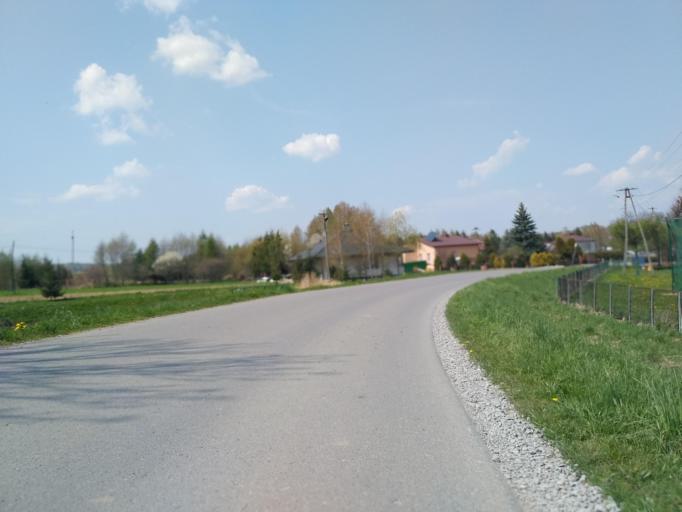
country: PL
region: Subcarpathian Voivodeship
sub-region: Powiat jasielski
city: Tarnowiec
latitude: 49.6678
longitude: 21.5652
